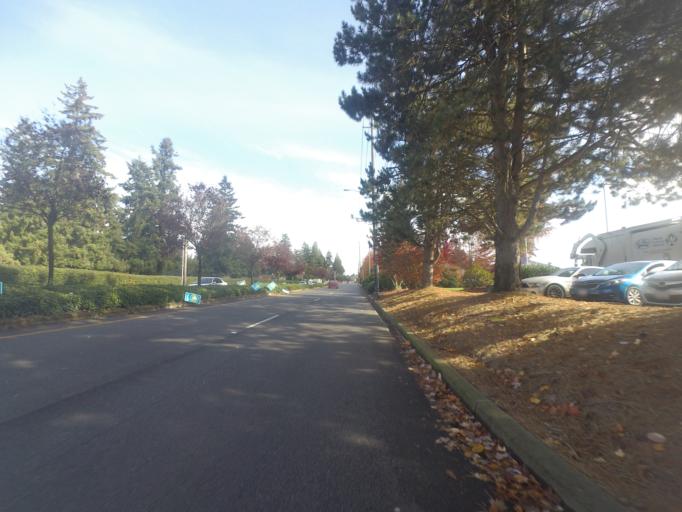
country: US
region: Washington
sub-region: Pierce County
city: Lakewood
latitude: 47.1763
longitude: -122.4969
